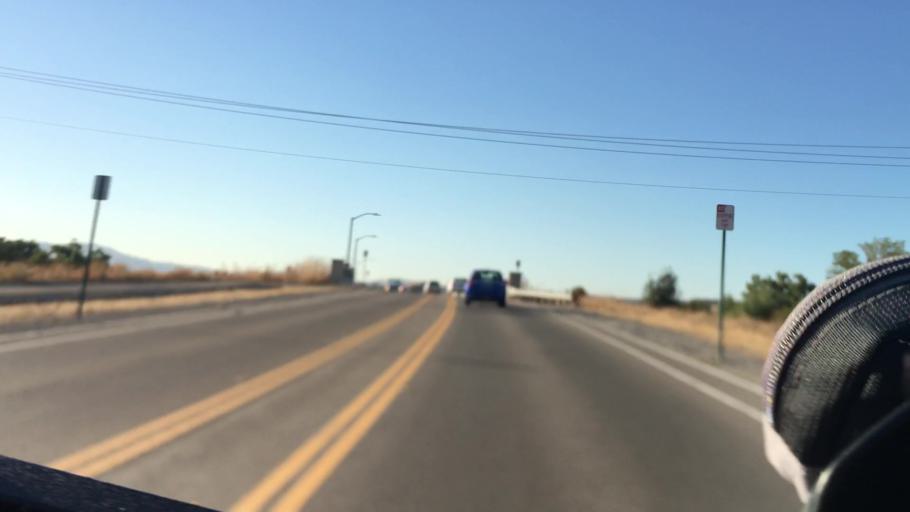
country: US
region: California
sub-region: Alameda County
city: Pleasanton
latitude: 37.6943
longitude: -121.8383
